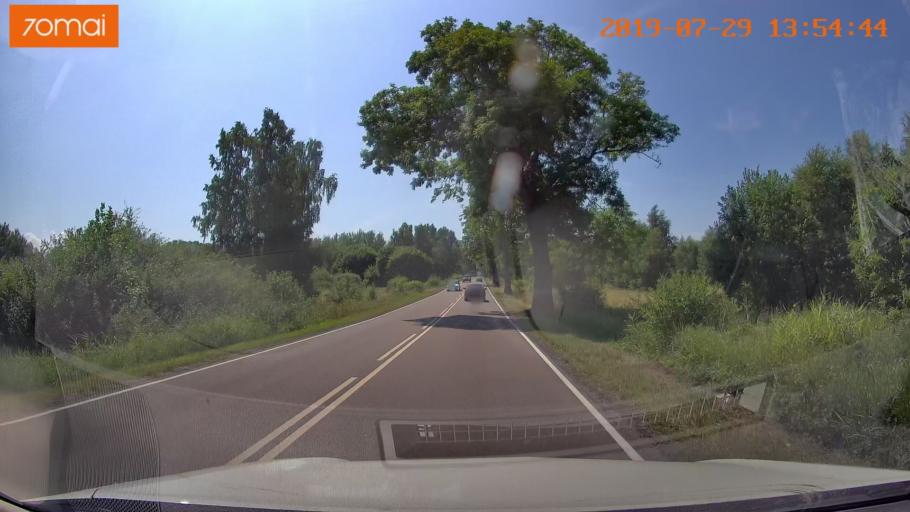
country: RU
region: Kaliningrad
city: Primorsk
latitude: 54.7206
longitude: 19.9635
